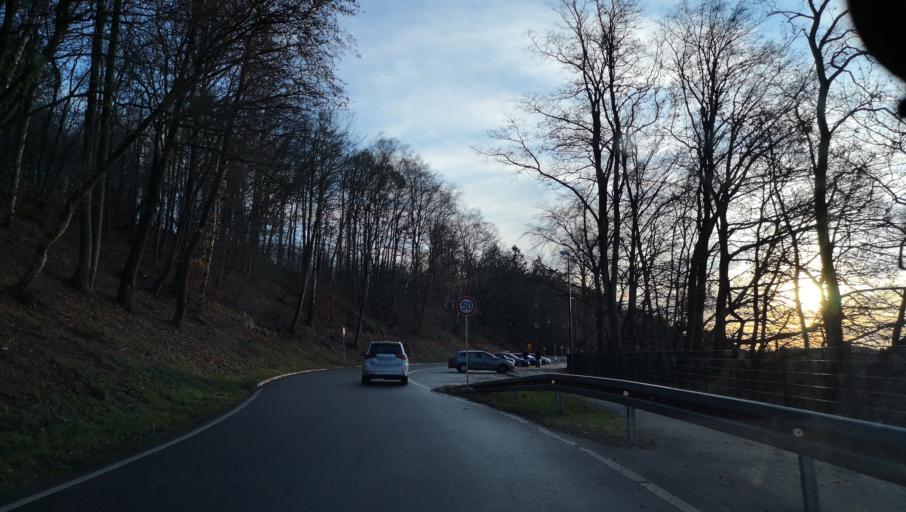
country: DE
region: North Rhine-Westphalia
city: Huckeswagen
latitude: 51.1420
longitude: 7.3742
